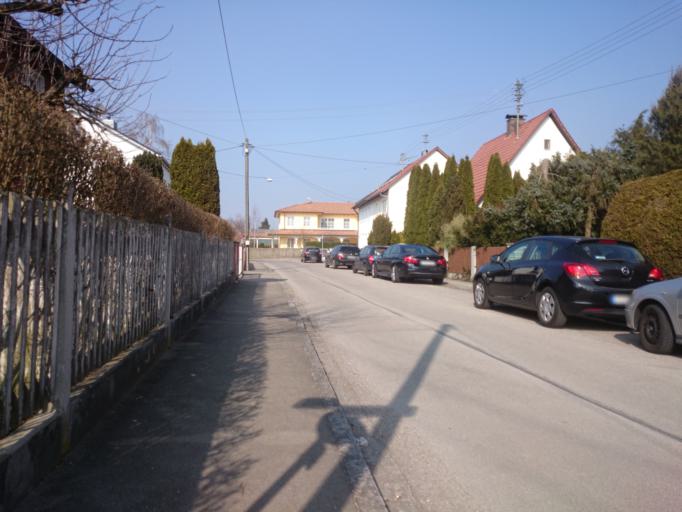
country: DE
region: Bavaria
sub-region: Swabia
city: Konigsbrunn
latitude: 48.2879
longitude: 10.8999
